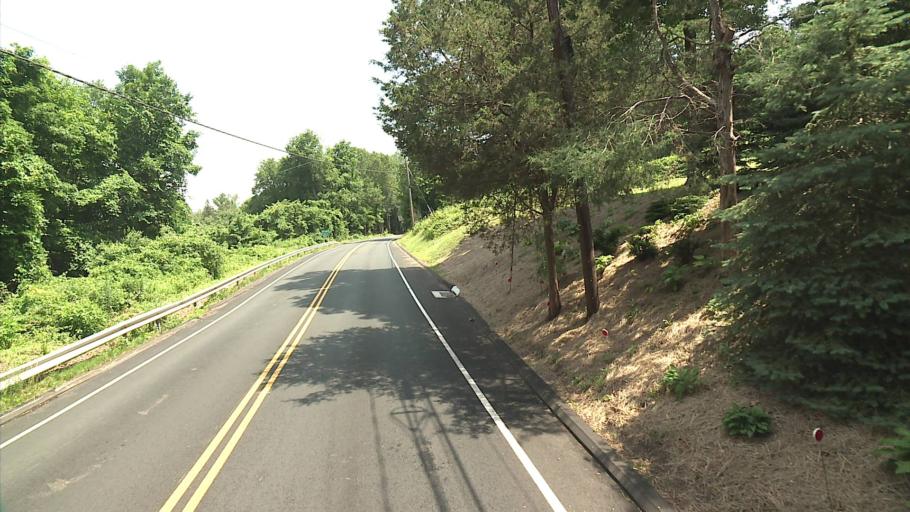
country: US
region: Connecticut
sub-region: New Haven County
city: Branford
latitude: 41.3190
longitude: -72.8189
